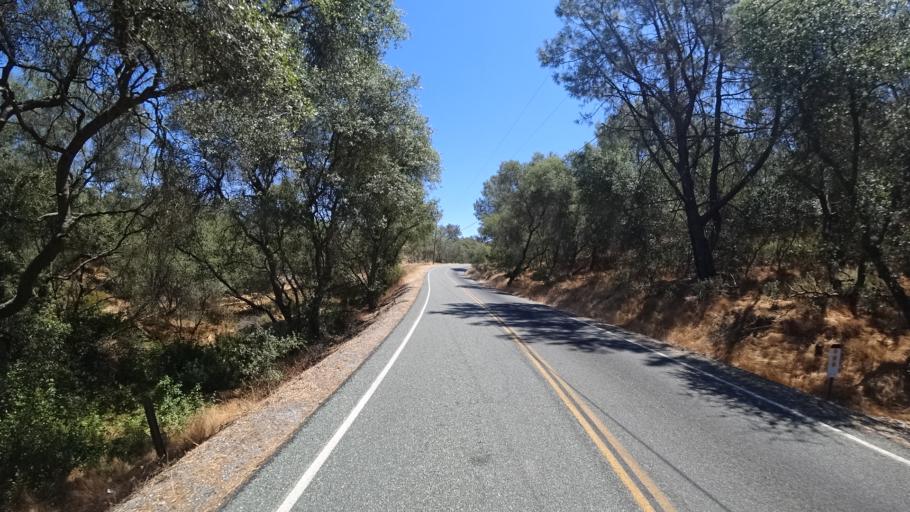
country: US
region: California
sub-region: Calaveras County
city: Valley Springs
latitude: 38.2124
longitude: -120.9120
